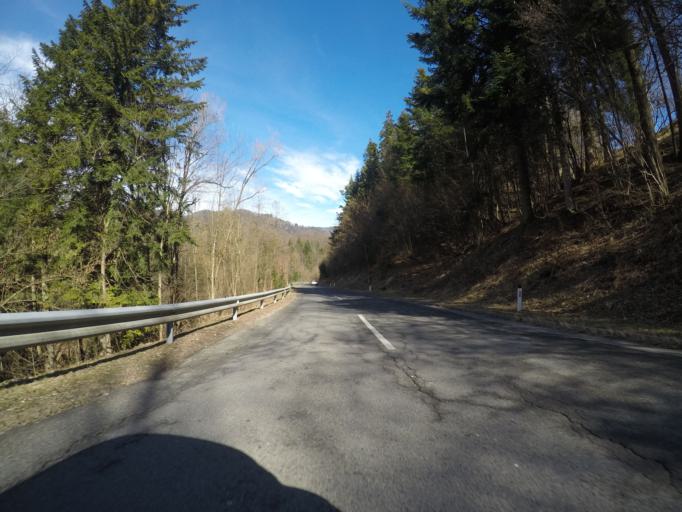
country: SI
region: Lovrenc na Pohorju
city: Lovrenc na Pohorju
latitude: 46.5412
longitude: 15.4392
